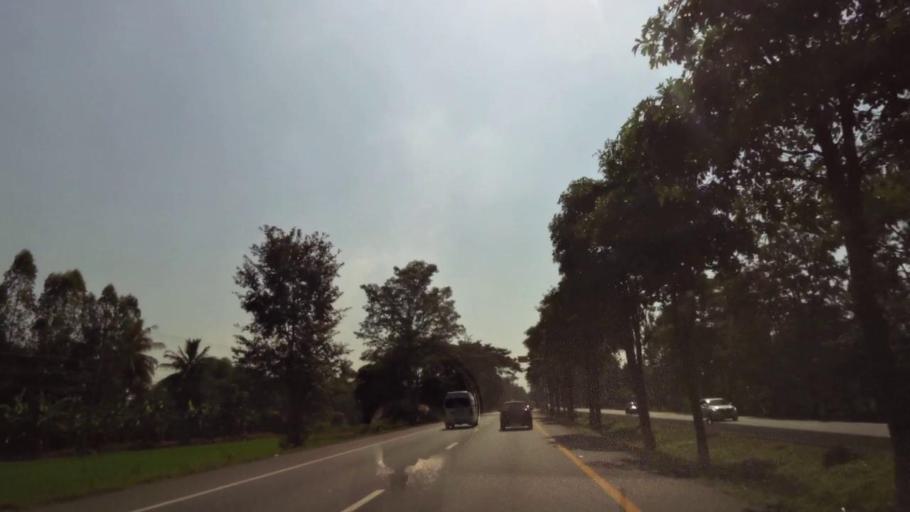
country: TH
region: Phichit
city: Bueng Na Rang
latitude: 16.0653
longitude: 100.1235
